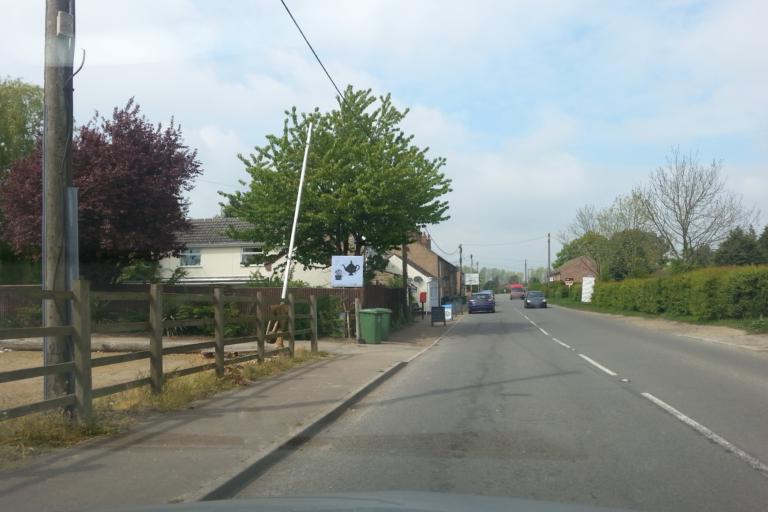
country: GB
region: England
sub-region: Norfolk
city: Outwell
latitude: 52.5797
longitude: 0.2205
